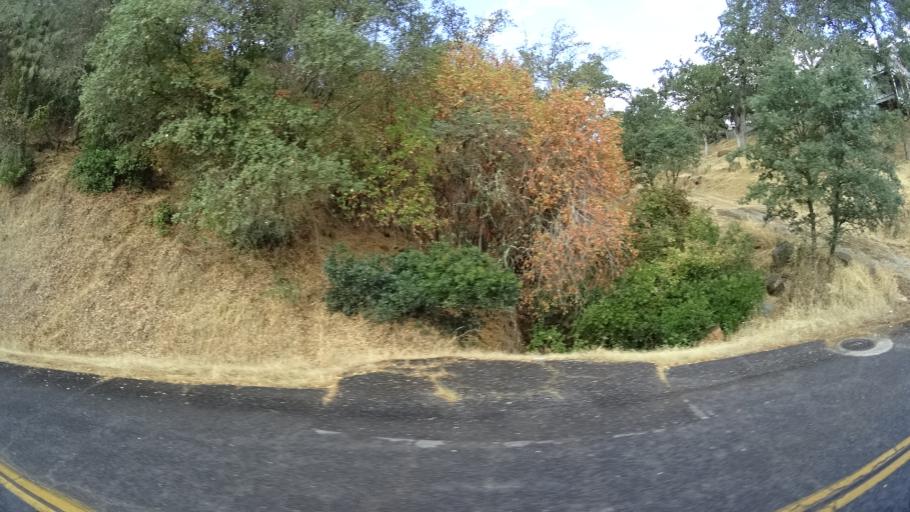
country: US
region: California
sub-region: Calaveras County
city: Copperopolis
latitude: 37.9102
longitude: -120.6050
